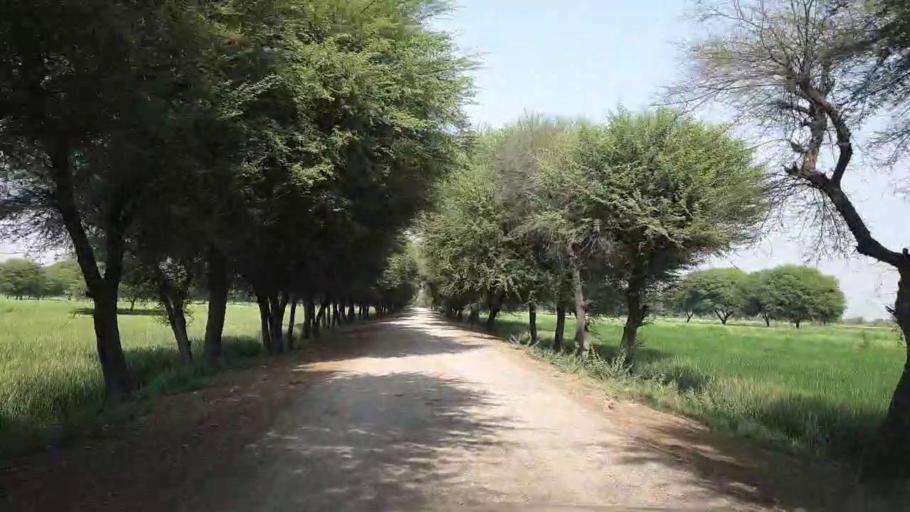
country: PK
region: Sindh
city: Dhoro Naro
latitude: 25.4775
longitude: 69.6191
